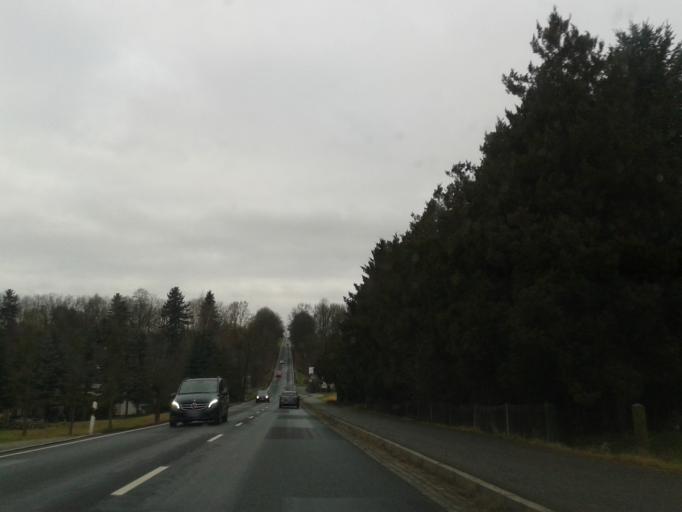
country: DE
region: Saxony
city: Niedercunnersdorf
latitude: 51.0746
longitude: 14.6534
